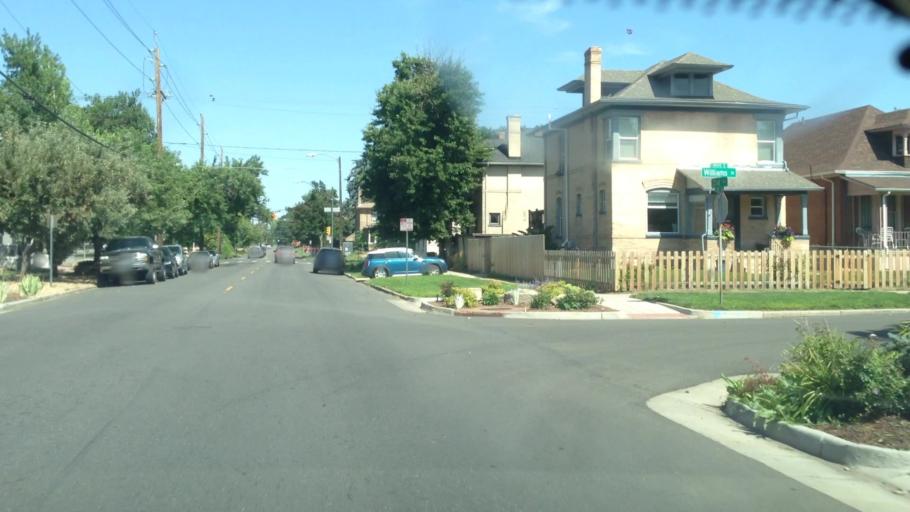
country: US
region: Colorado
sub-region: Denver County
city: Denver
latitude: 39.7507
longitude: -104.9661
